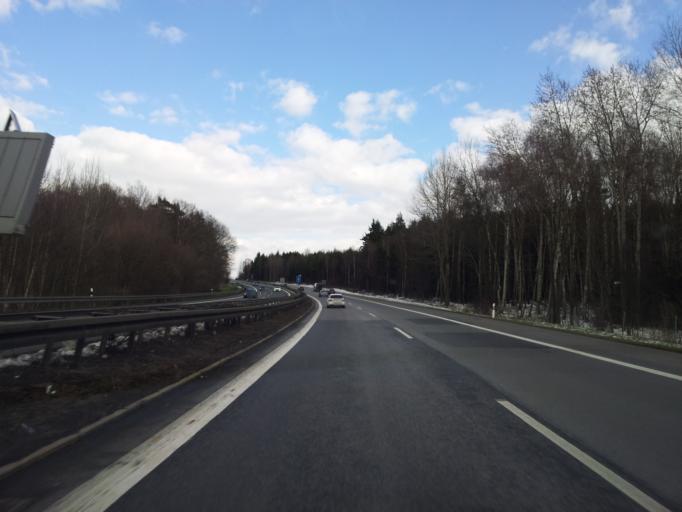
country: DE
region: Saxony
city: Hirschfeld
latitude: 50.6484
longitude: 12.4781
